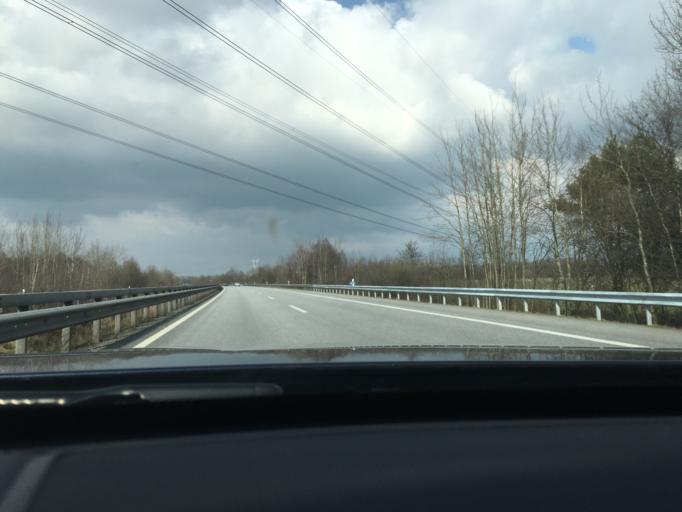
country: DE
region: Lower Saxony
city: Uthlede
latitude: 53.3243
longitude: 8.6195
